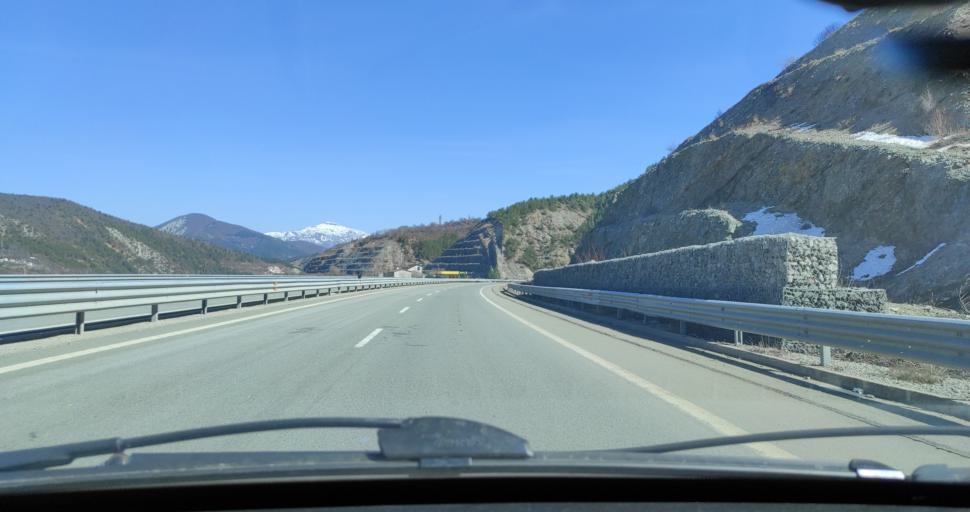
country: AL
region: Lezhe
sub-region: Rrethi i Lezhes
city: Shengjin
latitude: 41.9162
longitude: 20.1402
